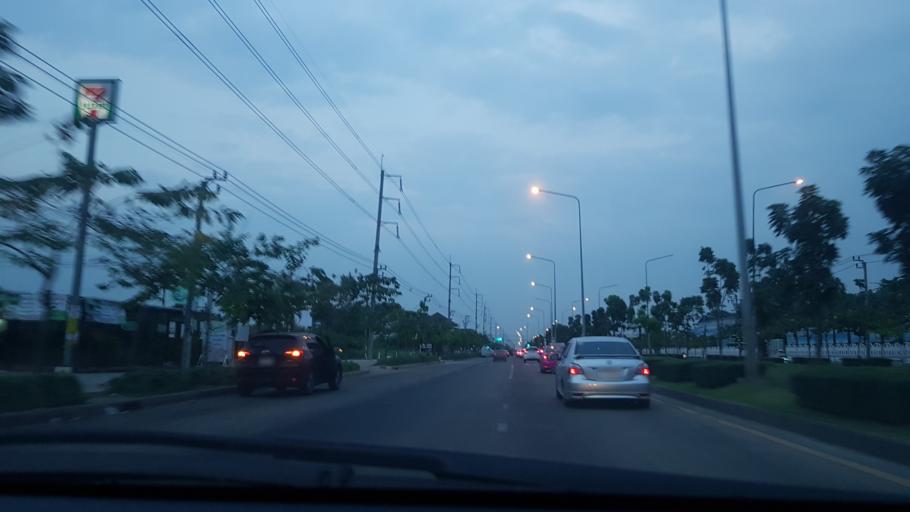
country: TH
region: Bangkok
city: Nong Khaem
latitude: 13.7327
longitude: 100.3638
